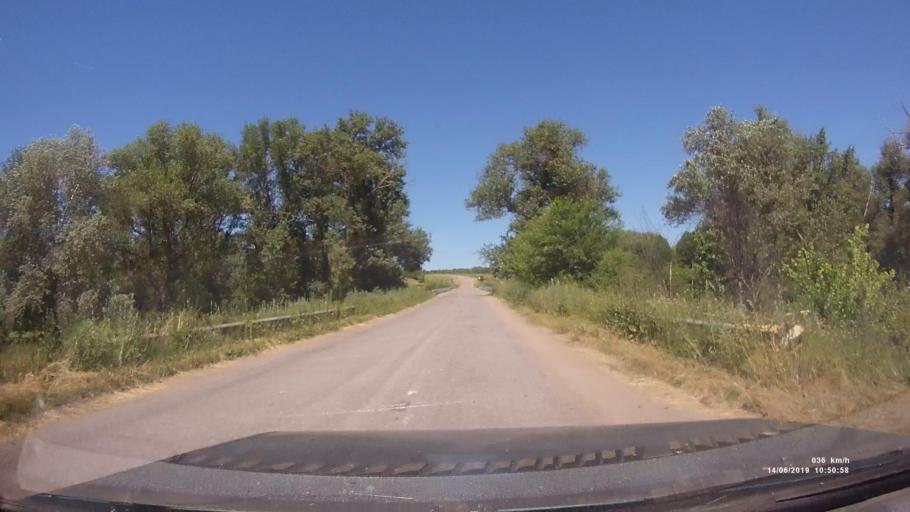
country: RU
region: Rostov
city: Kazanskaya
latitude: 49.8680
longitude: 41.3954
